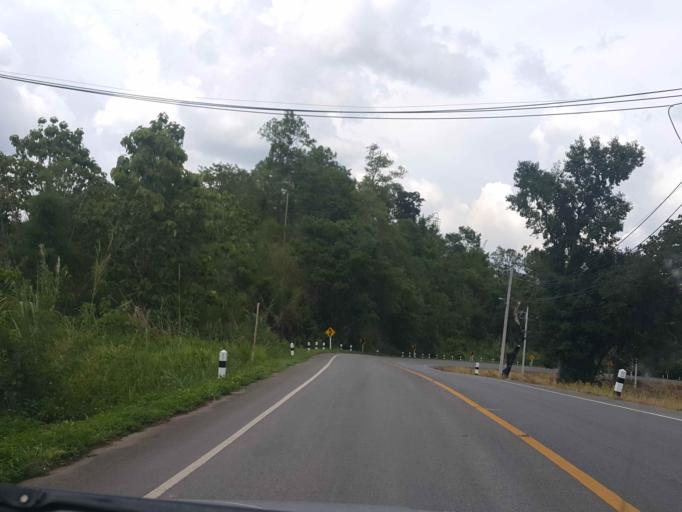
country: TH
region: Nan
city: Ban Luang
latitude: 18.8756
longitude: 100.5689
